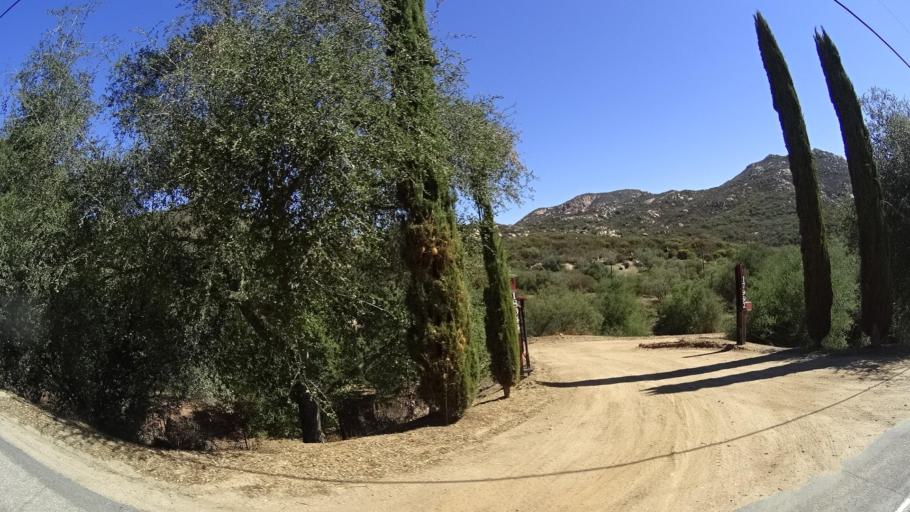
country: US
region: California
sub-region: San Diego County
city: Alpine
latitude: 32.7231
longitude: -116.7606
